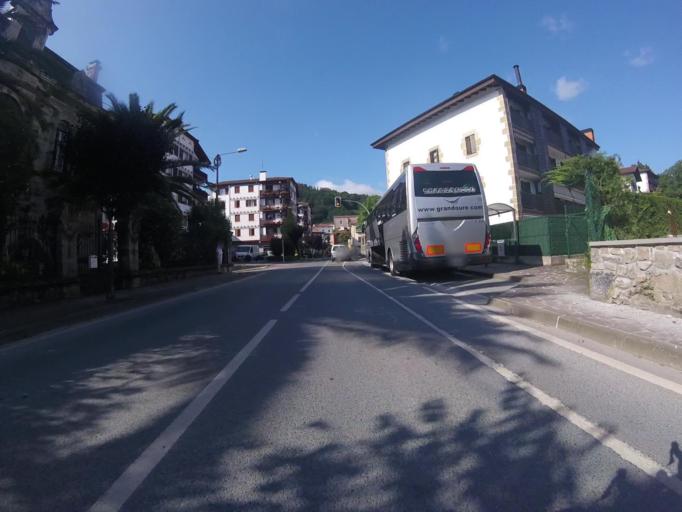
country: ES
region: Navarre
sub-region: Provincia de Navarra
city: Bera
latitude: 43.2793
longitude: -1.6884
